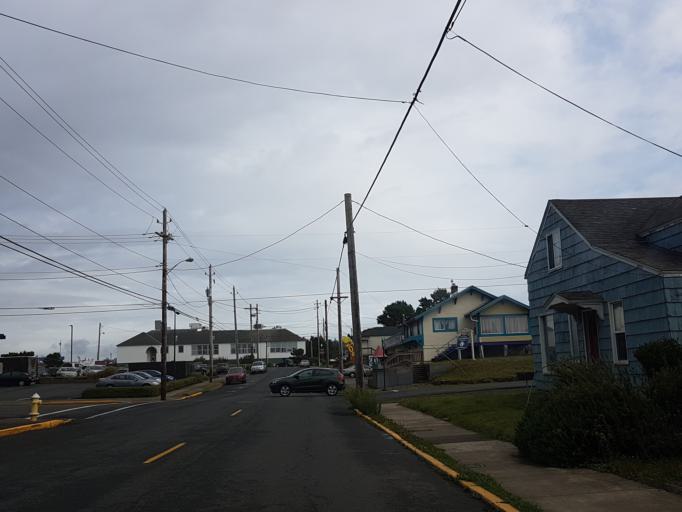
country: US
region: Oregon
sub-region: Lincoln County
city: Newport
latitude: 44.6330
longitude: -124.0553
